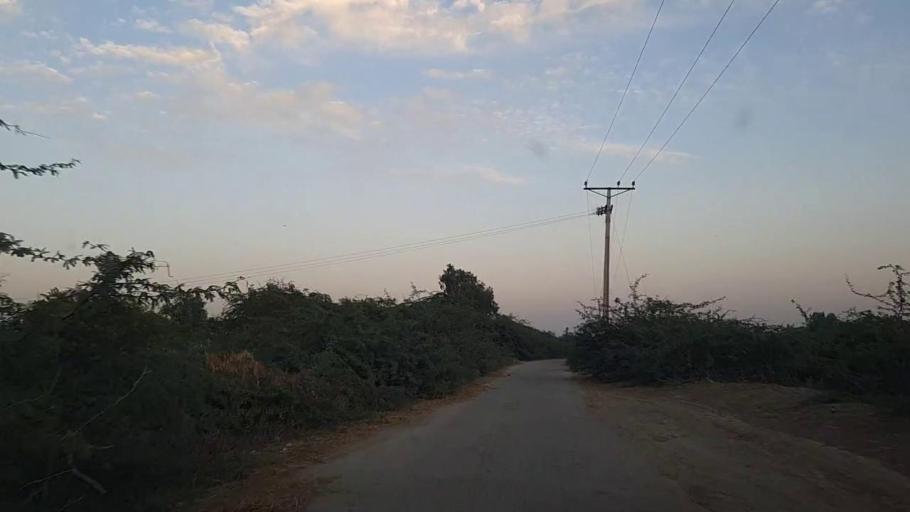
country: PK
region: Sindh
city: Thatta
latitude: 24.7980
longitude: 67.9473
